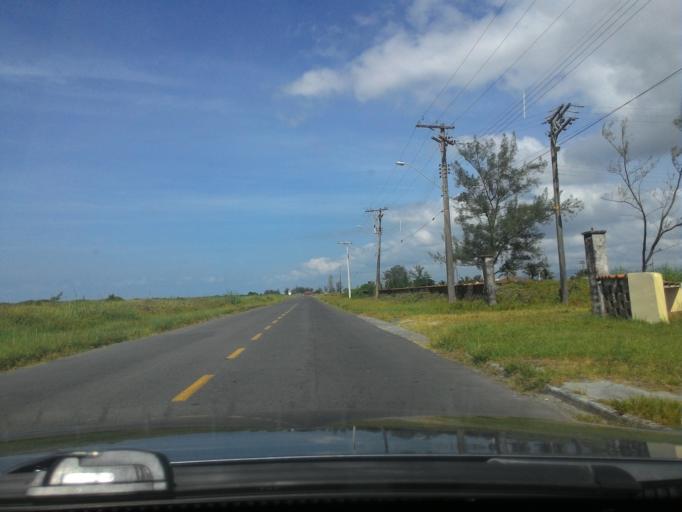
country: BR
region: Sao Paulo
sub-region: Iguape
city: Iguape
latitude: -24.7997
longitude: -47.6282
